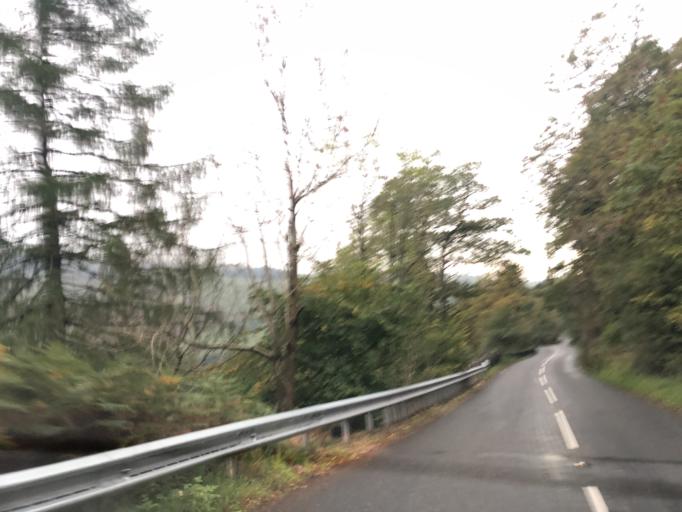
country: GB
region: England
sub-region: Cumbria
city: Windermere
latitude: 54.4338
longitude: -2.9020
